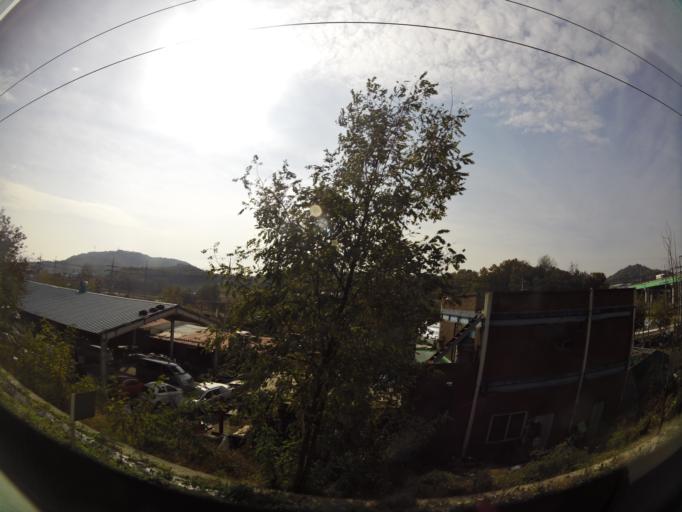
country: KR
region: Daejeon
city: Songgang-dong
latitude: 36.5383
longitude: 127.3426
